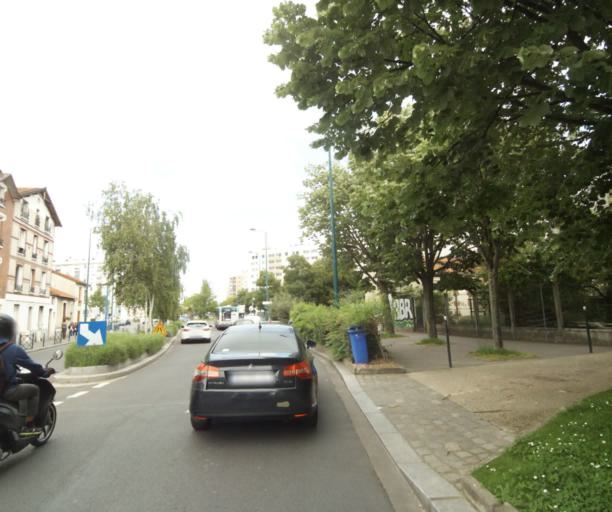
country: FR
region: Ile-de-France
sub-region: Departement des Hauts-de-Seine
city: Asnieres-sur-Seine
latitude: 48.9222
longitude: 2.2854
